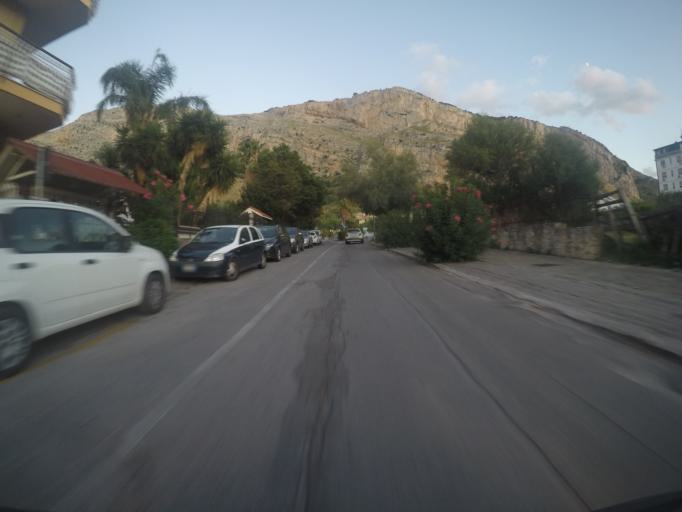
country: IT
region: Sicily
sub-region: Palermo
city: Capaci
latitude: 38.1795
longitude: 13.2438
